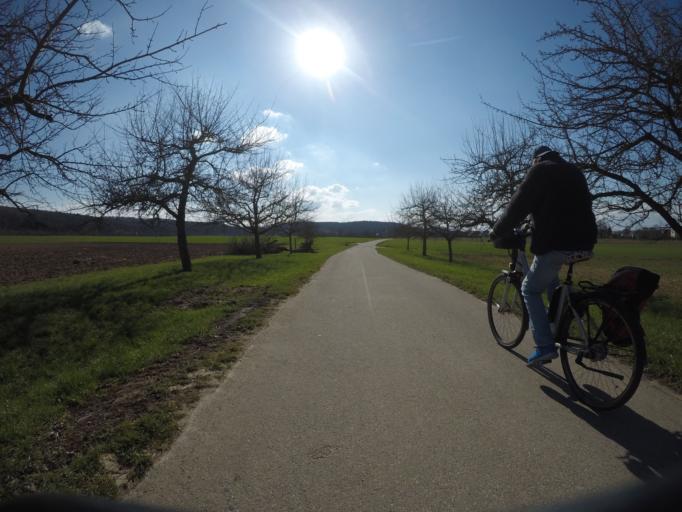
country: DE
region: Baden-Wuerttemberg
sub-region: Tuebingen Region
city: Tuebingen
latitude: 48.4948
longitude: 9.0405
